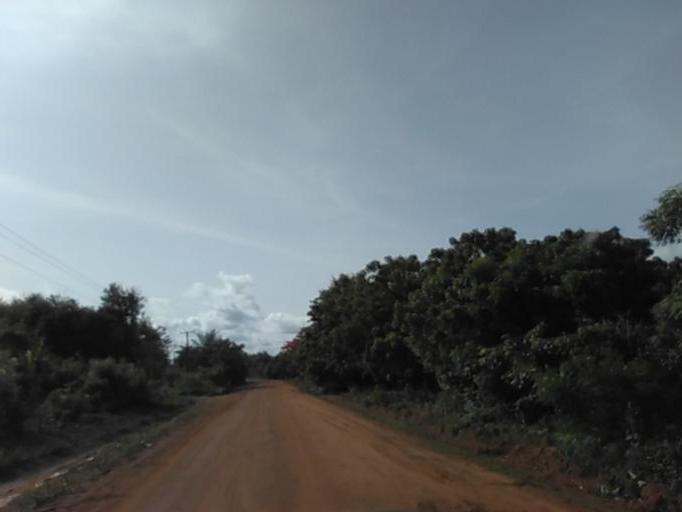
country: GH
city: Akropong
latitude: 6.0592
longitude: 0.2911
